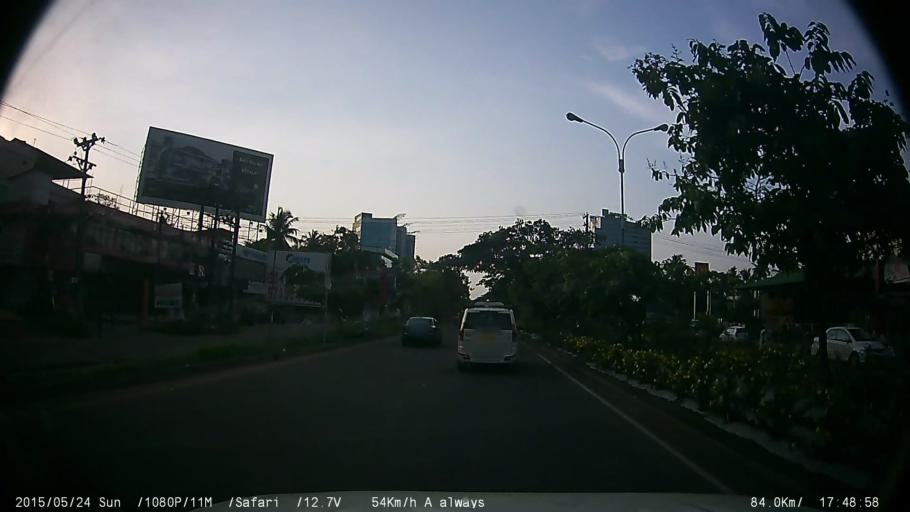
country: IN
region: Kerala
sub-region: Ernakulam
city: Cochin
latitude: 9.9869
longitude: 76.3160
